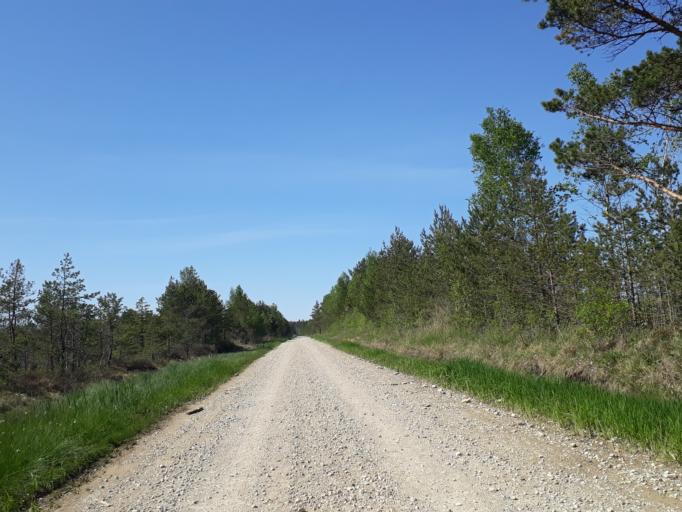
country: EE
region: Paernumaa
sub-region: Vaendra vald (alev)
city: Vandra
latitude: 58.7399
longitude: 24.9902
